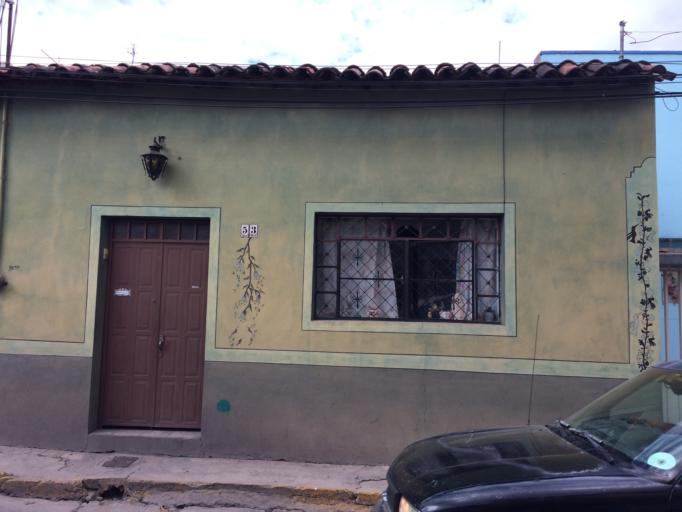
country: MX
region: Oaxaca
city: Ciudad de Huajuapam de Leon
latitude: 17.8077
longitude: -97.7792
